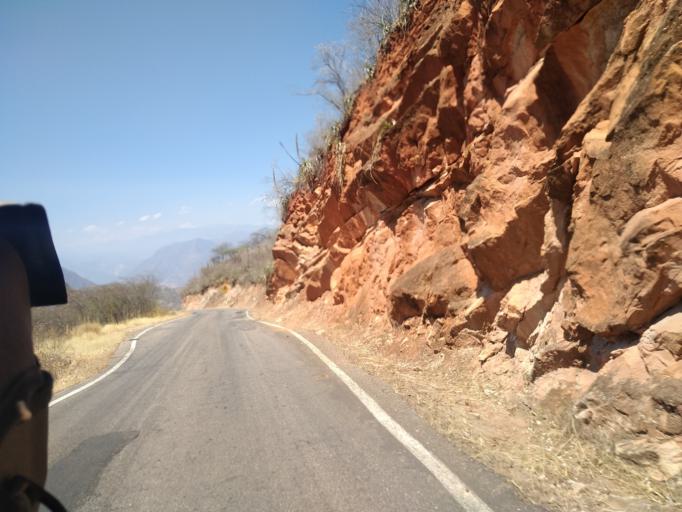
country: PE
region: Amazonas
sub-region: Provincia de Chachapoyas
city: Balsas
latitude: -6.8501
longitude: -77.9792
